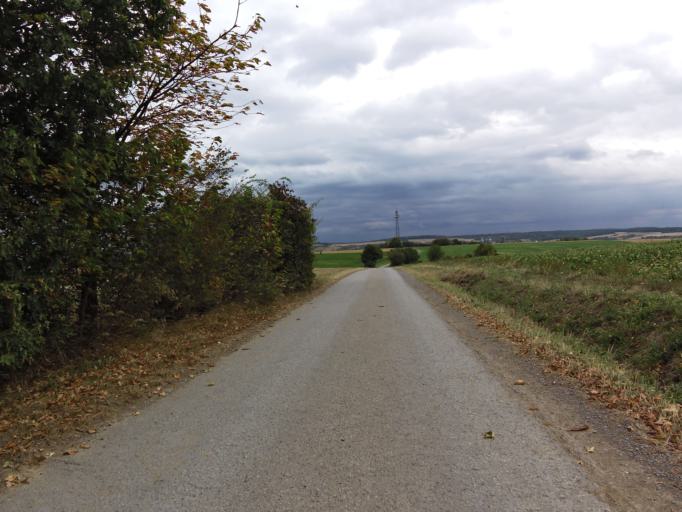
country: DE
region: Bavaria
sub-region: Regierungsbezirk Unterfranken
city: Rimpar
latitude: 49.8345
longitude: 9.9421
